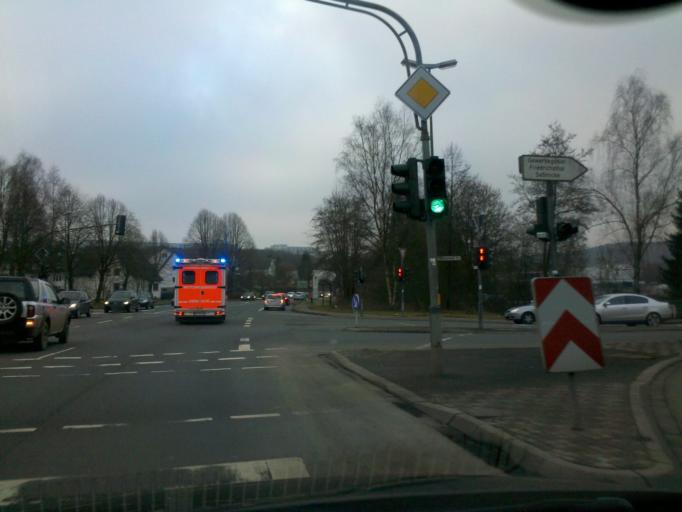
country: DE
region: North Rhine-Westphalia
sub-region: Regierungsbezirk Arnsberg
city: Olpe
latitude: 51.0039
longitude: 7.8416
